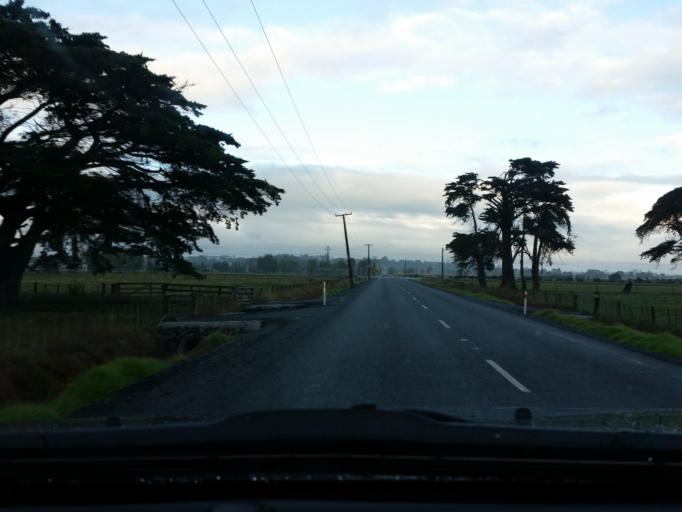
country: NZ
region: Northland
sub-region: Kaipara District
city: Dargaville
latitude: -35.9513
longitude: 173.8958
